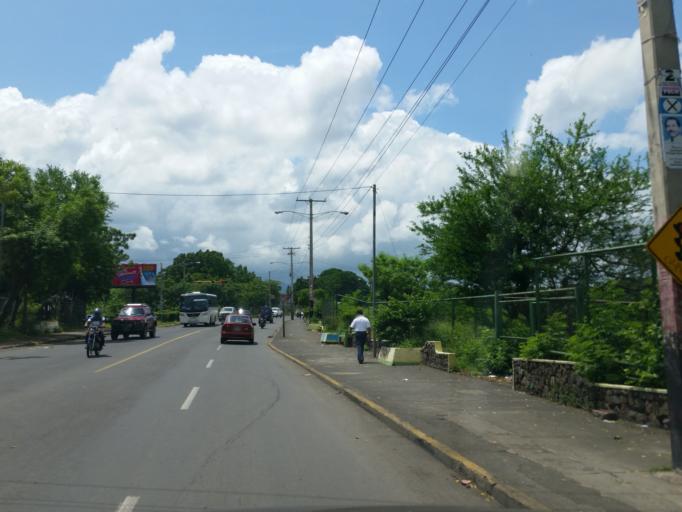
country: NI
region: Managua
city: Managua
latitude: 12.1399
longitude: -86.2679
